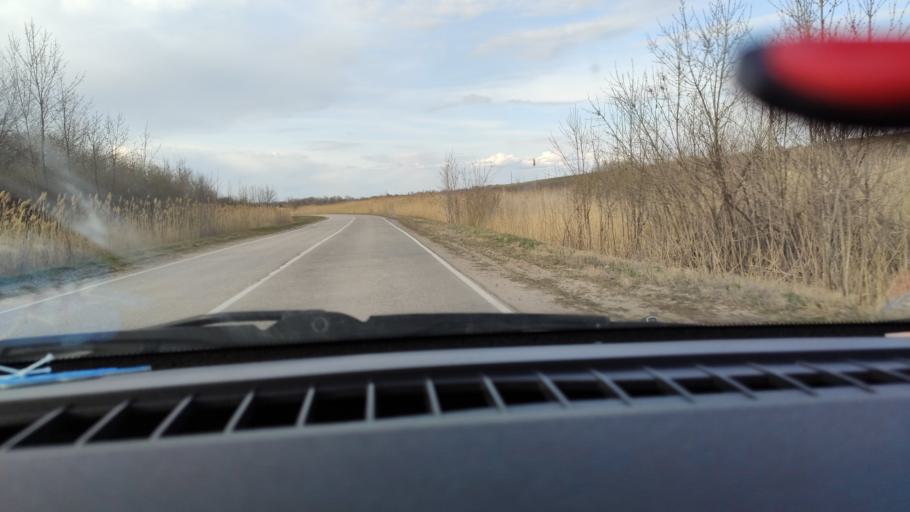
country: RU
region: Saratov
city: Privolzhskiy
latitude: 51.2643
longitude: 45.9460
